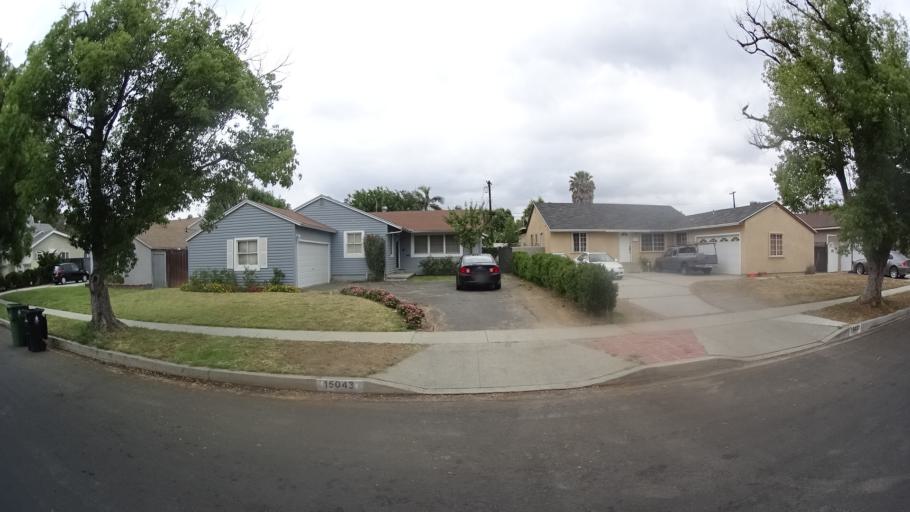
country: US
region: California
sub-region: Los Angeles County
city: San Fernando
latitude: 34.2601
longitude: -118.4602
